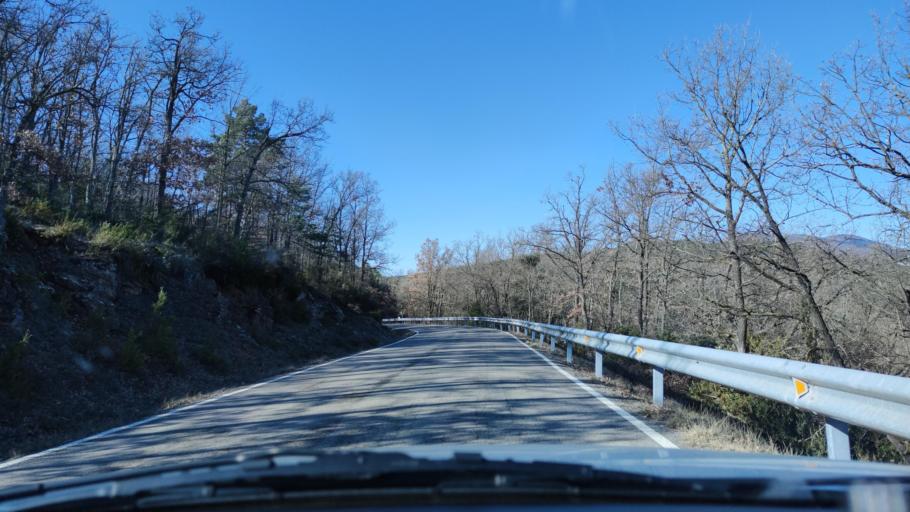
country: ES
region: Catalonia
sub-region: Provincia de Lleida
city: Artesa de Segre
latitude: 42.0462
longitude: 1.0721
